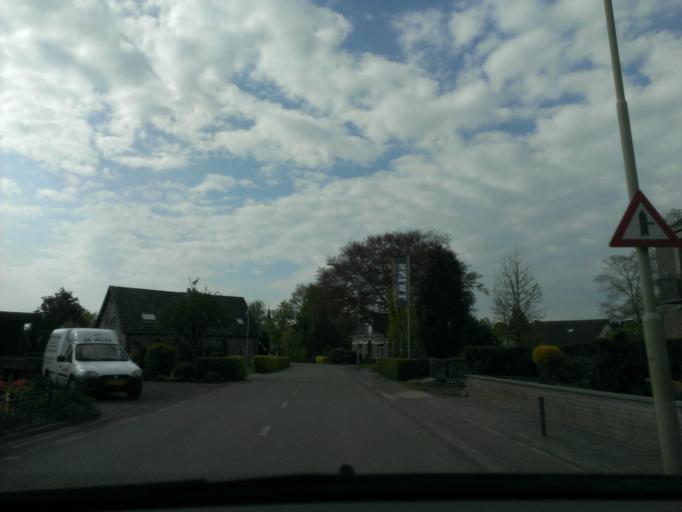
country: NL
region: Gelderland
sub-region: Gemeente Epe
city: Oene
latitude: 52.3423
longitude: 6.0501
